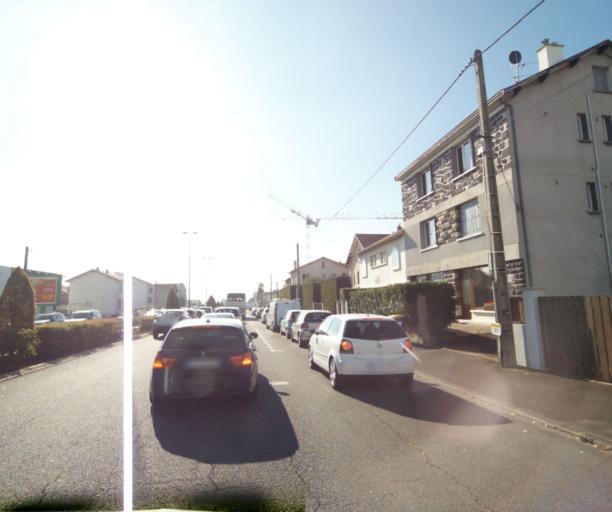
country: FR
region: Auvergne
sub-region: Departement du Puy-de-Dome
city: Aubiere
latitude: 45.7707
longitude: 3.1223
